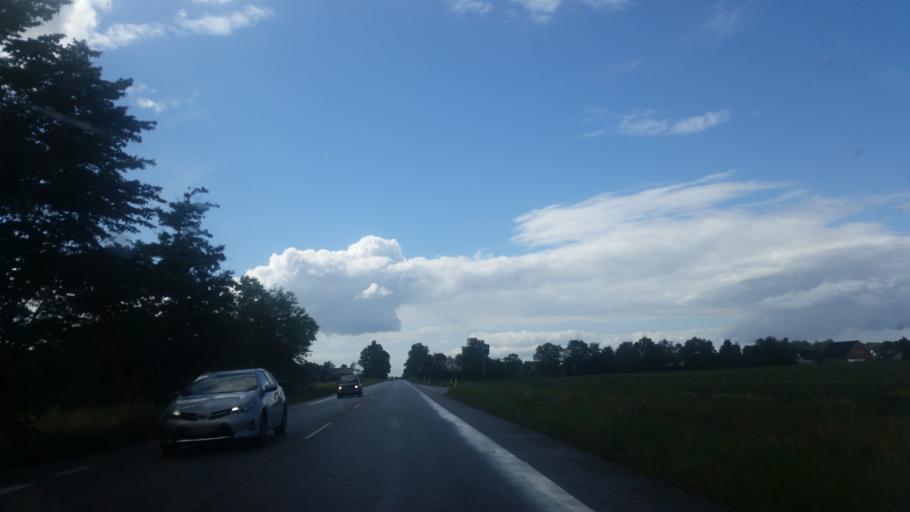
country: DK
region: Zealand
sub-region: Holbaek Kommune
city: Holbaek
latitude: 55.7223
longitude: 11.5967
